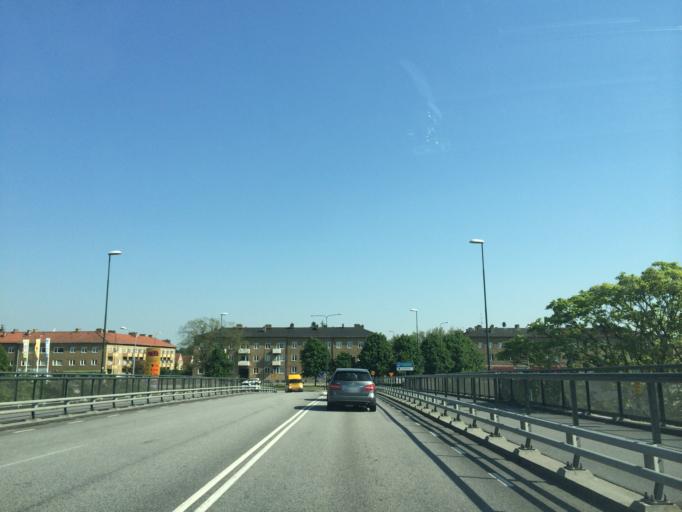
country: SE
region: Skane
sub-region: Burlovs Kommun
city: Arloev
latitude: 55.6156
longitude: 13.0415
